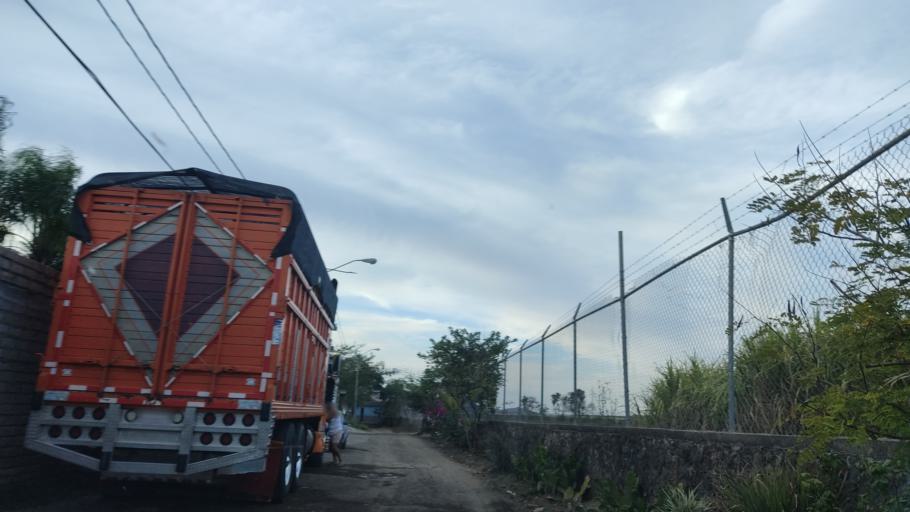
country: MX
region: Nayarit
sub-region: Tepic
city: La Corregidora
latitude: 21.4569
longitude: -104.8202
